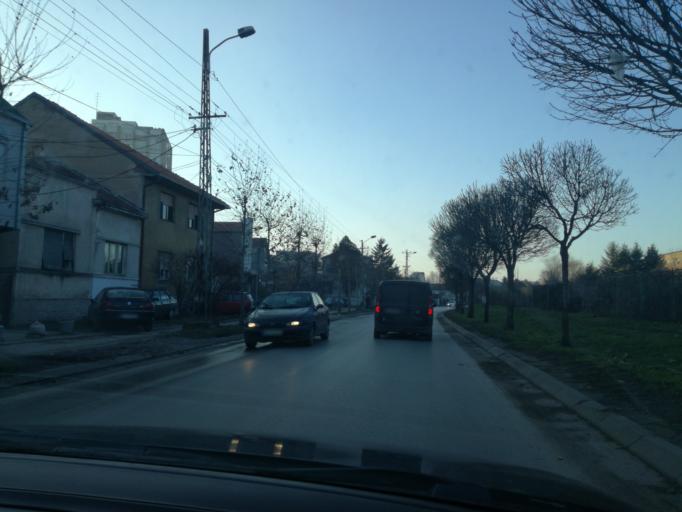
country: RS
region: Central Serbia
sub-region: Nisavski Okrug
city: Nis
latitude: 43.3124
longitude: 21.8898
